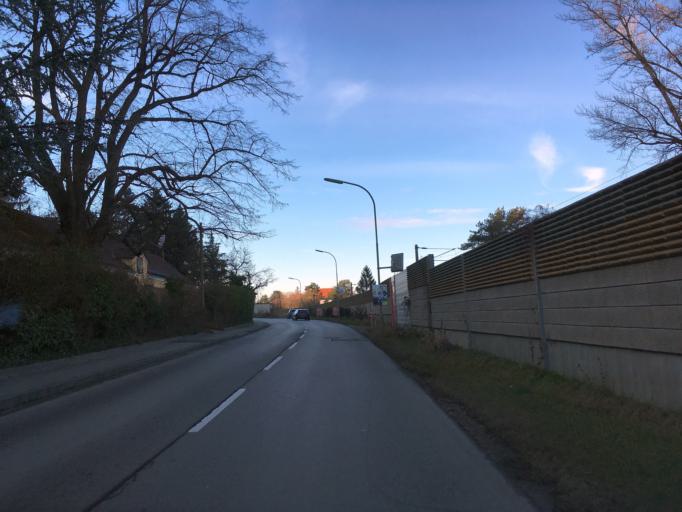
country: AT
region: Lower Austria
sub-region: Politischer Bezirk Korneuburg
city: Korneuburg
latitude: 48.3471
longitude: 16.2865
